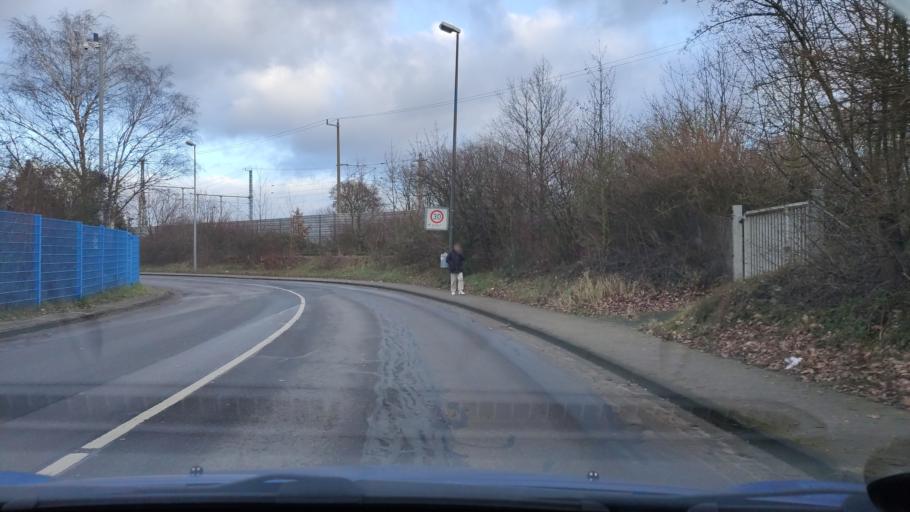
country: DE
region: Lower Saxony
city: Langenhagen
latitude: 52.4422
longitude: 9.7267
